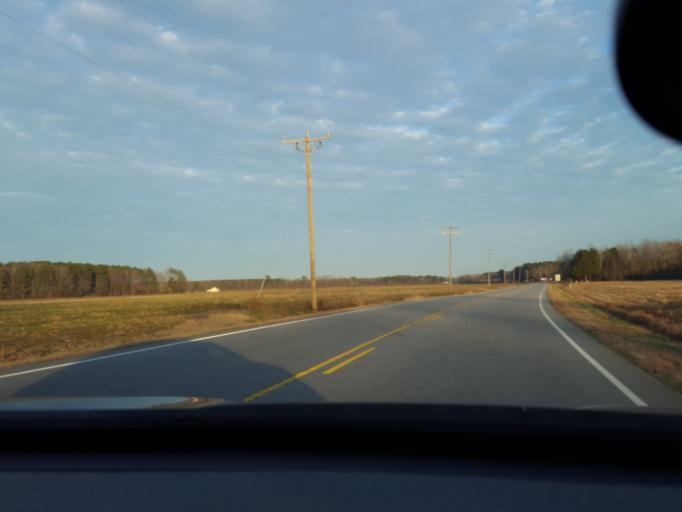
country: US
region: North Carolina
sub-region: Hertford County
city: Murfreesboro
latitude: 36.2881
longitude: -77.1872
